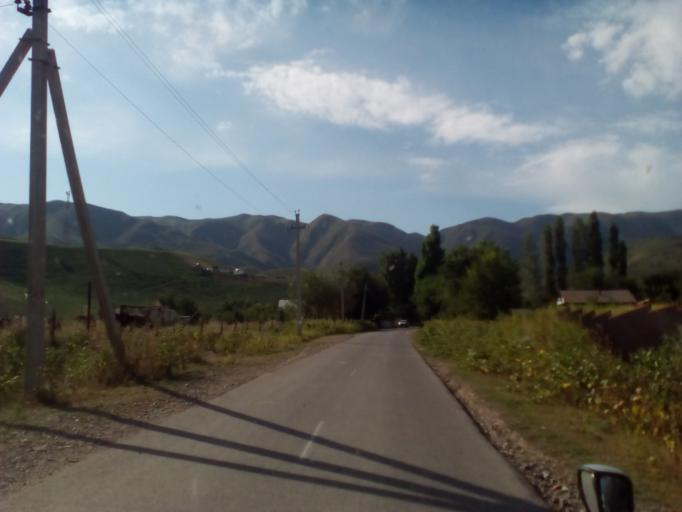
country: KZ
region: Almaty Oblysy
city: Burunday
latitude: 43.1557
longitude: 76.3848
